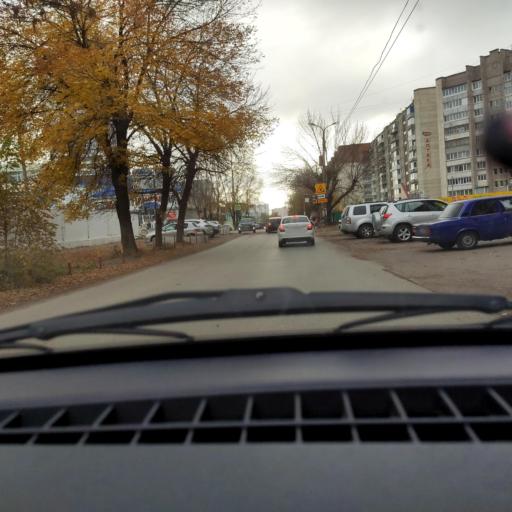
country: RU
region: Bashkortostan
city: Ufa
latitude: 54.7377
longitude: 55.9885
